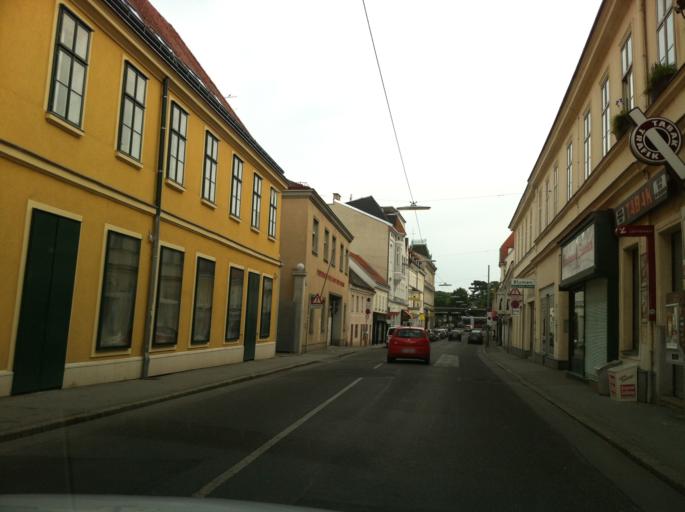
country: AT
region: Vienna
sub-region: Wien Stadt
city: Vienna
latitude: 48.1897
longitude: 16.3046
